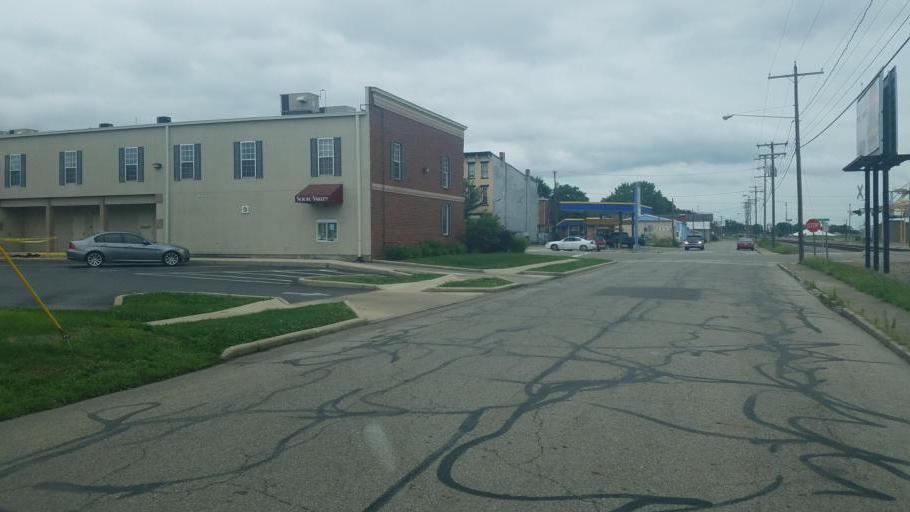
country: US
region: Ohio
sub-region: Pickaway County
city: Circleville
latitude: 39.6035
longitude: -82.9483
